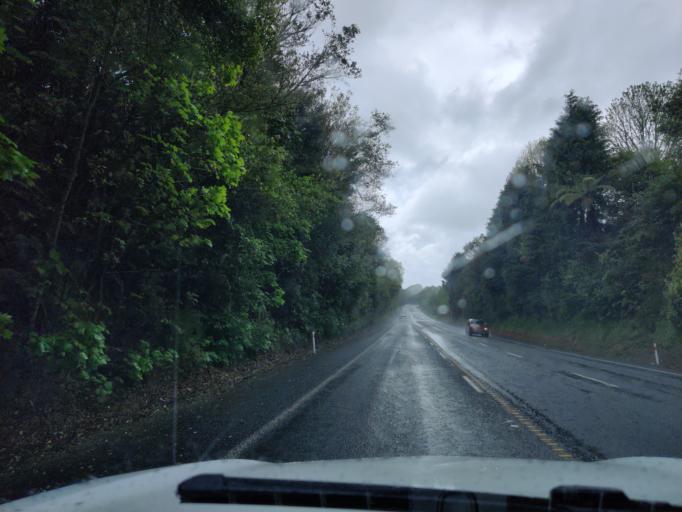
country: NZ
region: Bay of Plenty
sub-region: Rotorua District
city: Rotorua
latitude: -38.0751
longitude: 176.1641
